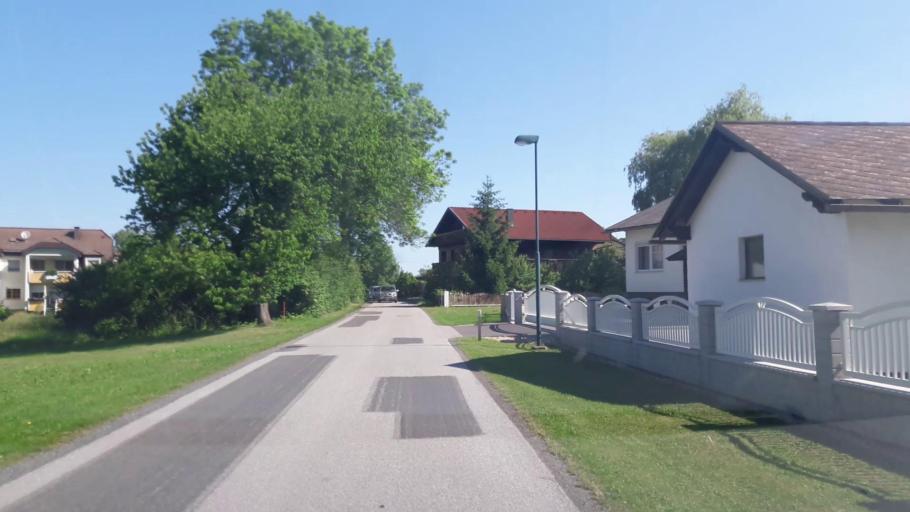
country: AT
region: Burgenland
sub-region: Politischer Bezirk Jennersdorf
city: Deutsch Kaltenbrunn
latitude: 47.0880
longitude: 16.1092
